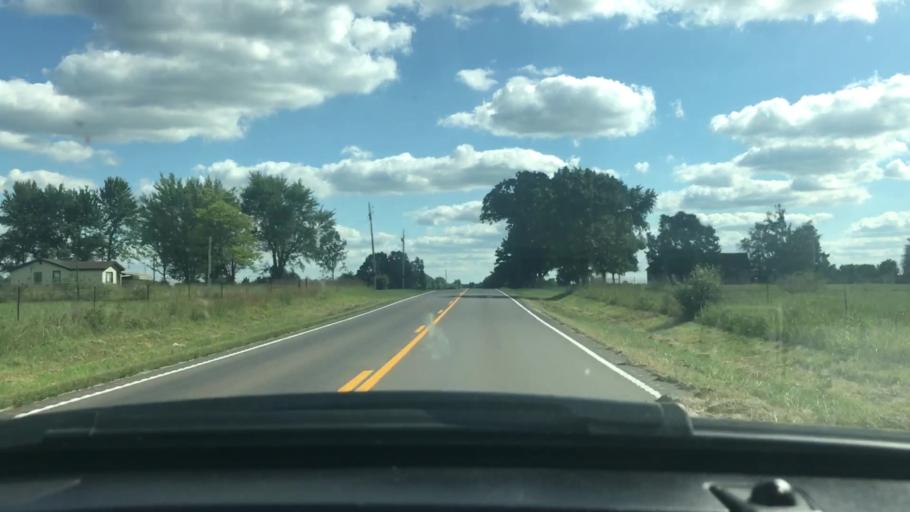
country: US
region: Missouri
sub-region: Wright County
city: Mountain Grove
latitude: 37.2634
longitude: -92.3081
